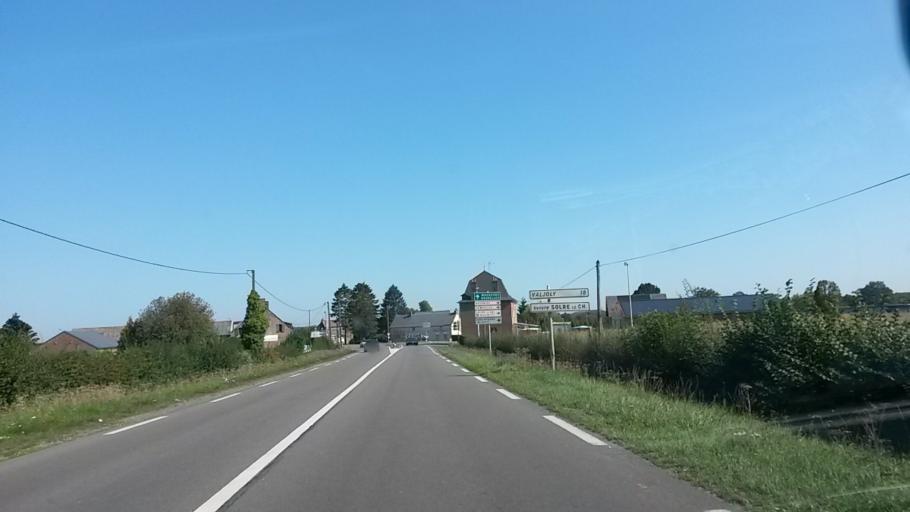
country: FR
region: Nord-Pas-de-Calais
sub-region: Departement du Nord
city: Avesnelles
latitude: 50.1533
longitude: 3.9539
